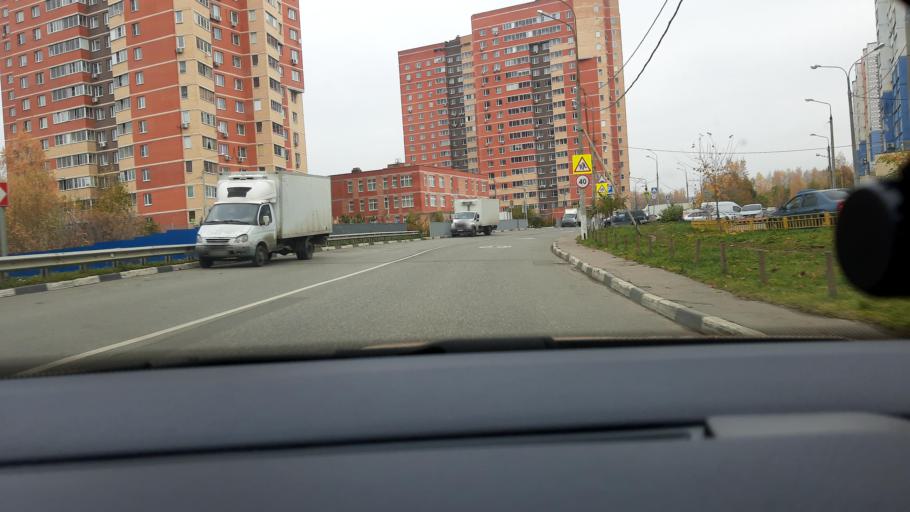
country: RU
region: Moskovskaya
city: Cherkizovo
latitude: 55.9448
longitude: 37.7754
